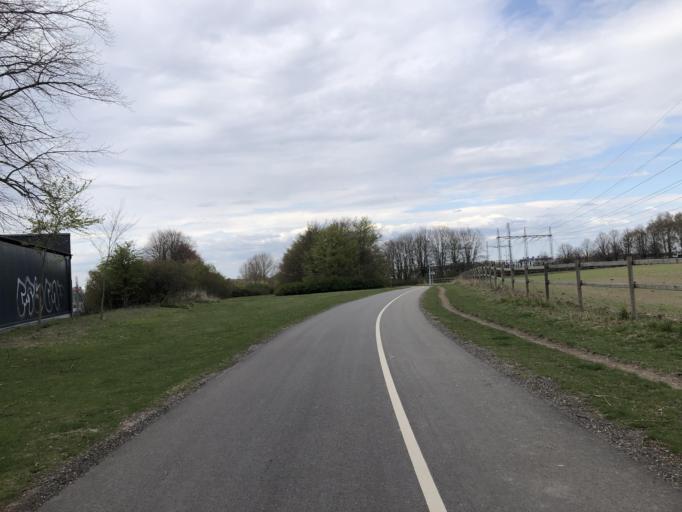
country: SE
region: Skane
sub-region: Malmo
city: Tygelsjo
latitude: 55.5593
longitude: 13.0407
